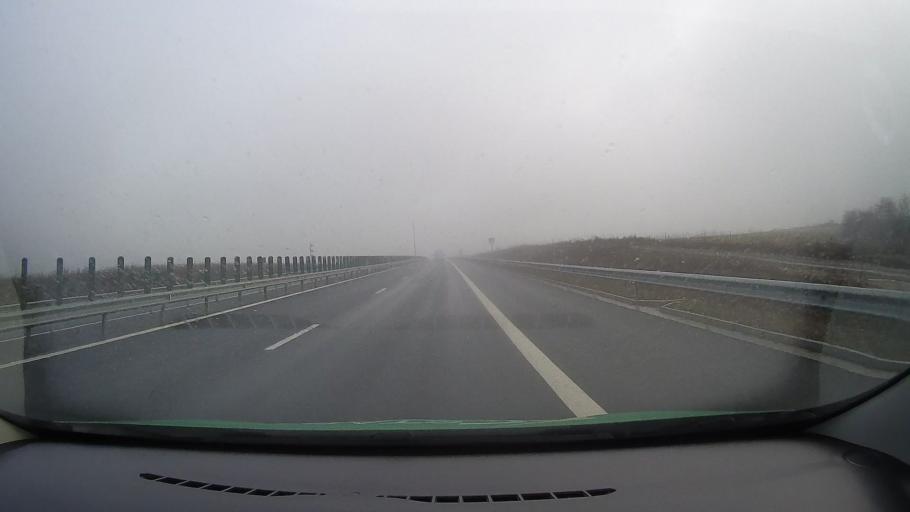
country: RO
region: Timis
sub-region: Comuna Faget
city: Faget
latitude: 45.8316
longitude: 22.2068
